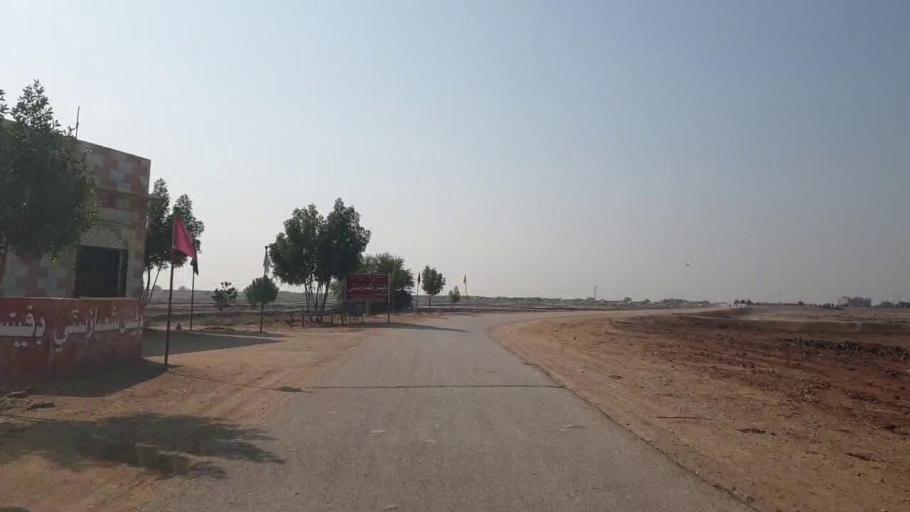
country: PK
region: Sindh
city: Sehwan
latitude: 26.4327
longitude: 67.8438
